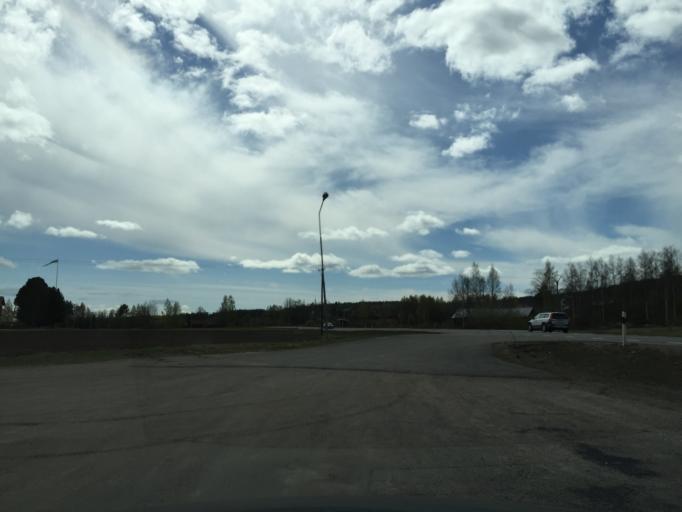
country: SE
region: Gaevleborg
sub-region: Bollnas Kommun
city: Arbra
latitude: 61.5044
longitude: 16.3576
